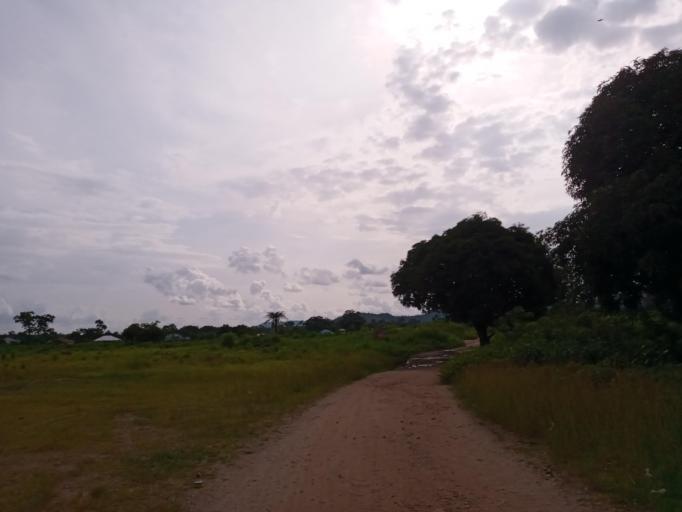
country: SL
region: Northern Province
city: Bumbuna
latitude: 9.0492
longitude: -11.7531
